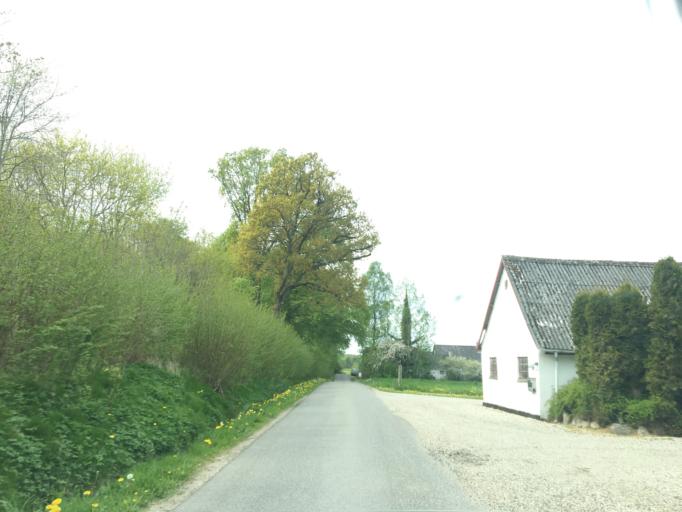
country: DK
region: Zealand
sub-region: Lejre Kommune
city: Osted
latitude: 55.5563
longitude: 11.9429
